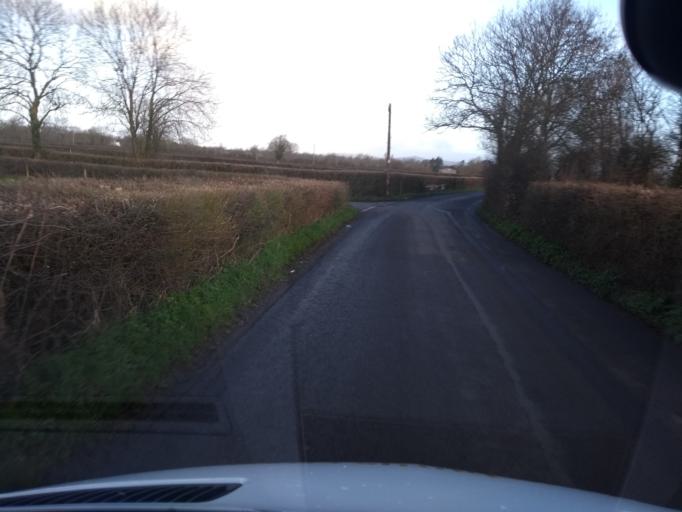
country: GB
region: England
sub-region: Somerset
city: Wedmore
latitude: 51.2387
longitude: -2.8219
